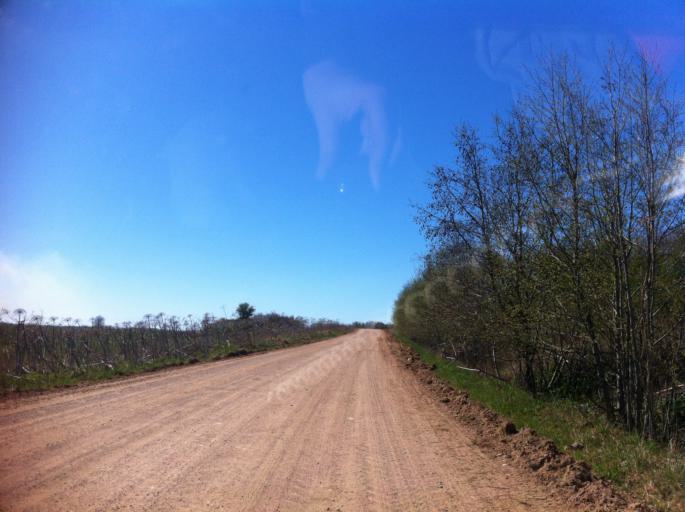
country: RU
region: Pskov
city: Izborsk
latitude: 57.8042
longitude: 27.9728
